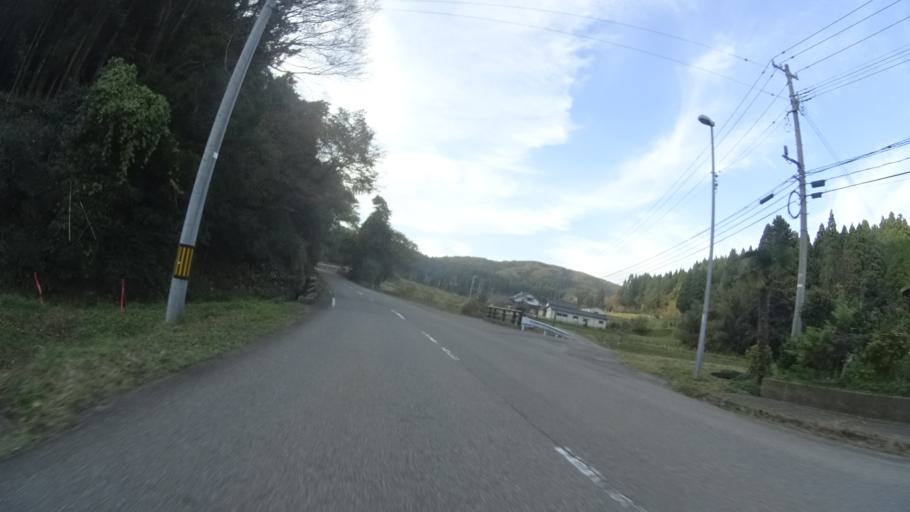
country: JP
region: Ishikawa
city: Nanao
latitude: 37.1939
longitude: 136.7162
